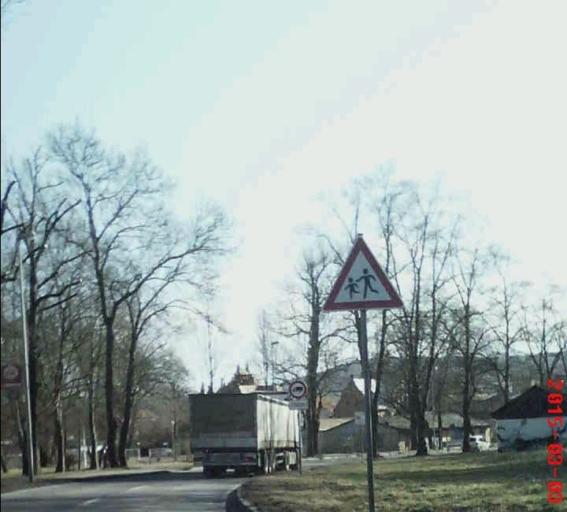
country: DE
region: Thuringia
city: Rudolstadt
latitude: 50.7146
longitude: 11.3122
